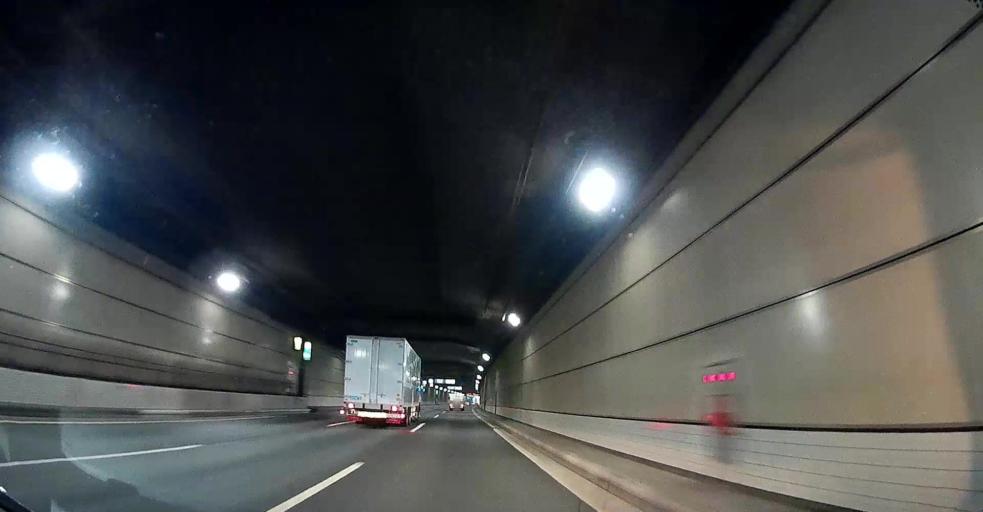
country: JP
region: Kanagawa
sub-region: Kawasaki-shi
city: Kawasaki
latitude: 35.5057
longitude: 139.7744
